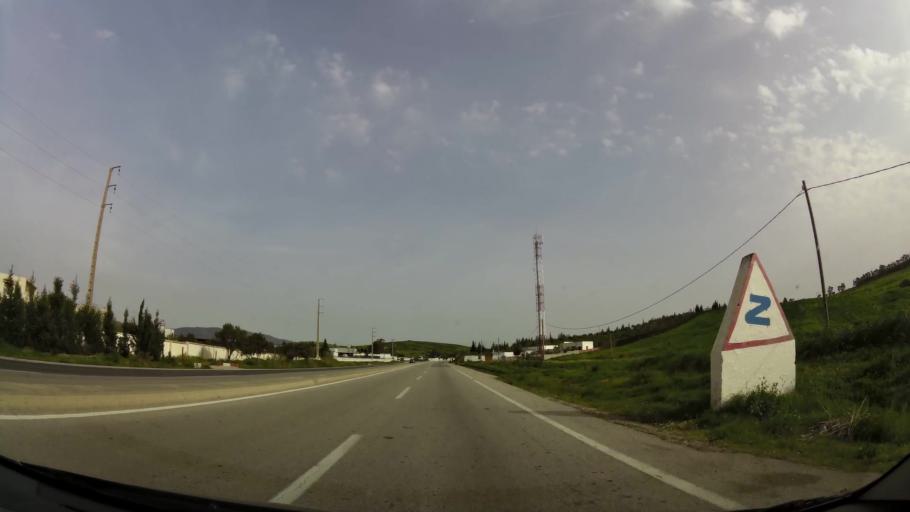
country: MA
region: Tanger-Tetouan
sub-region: Tanger-Assilah
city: Tangier
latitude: 35.6747
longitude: -5.7015
